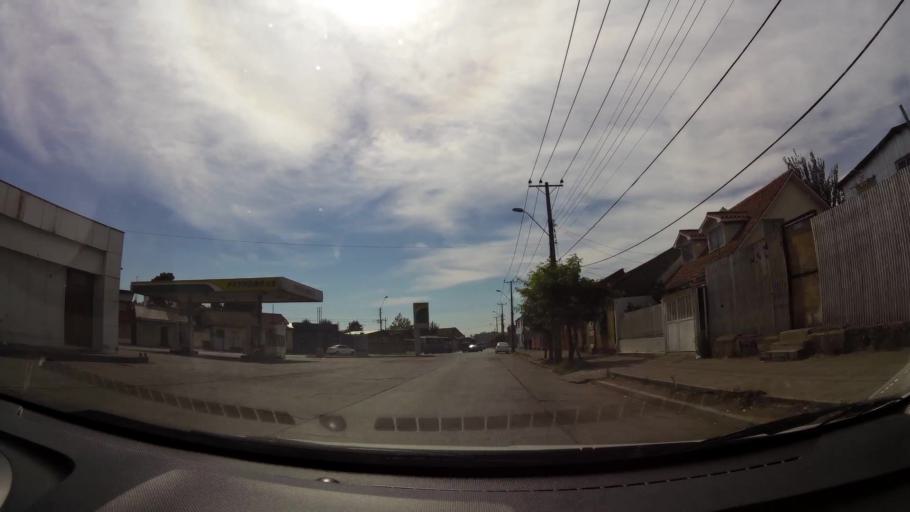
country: CL
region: Biobio
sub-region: Provincia de Concepcion
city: Talcahuano
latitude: -36.7253
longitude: -73.1202
